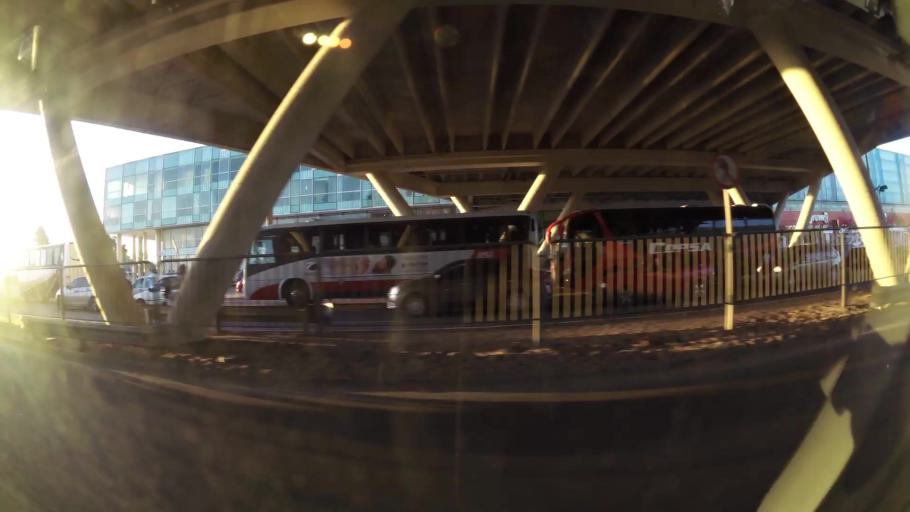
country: UY
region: Canelones
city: Barra de Carrasco
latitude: -34.8411
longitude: -55.9934
